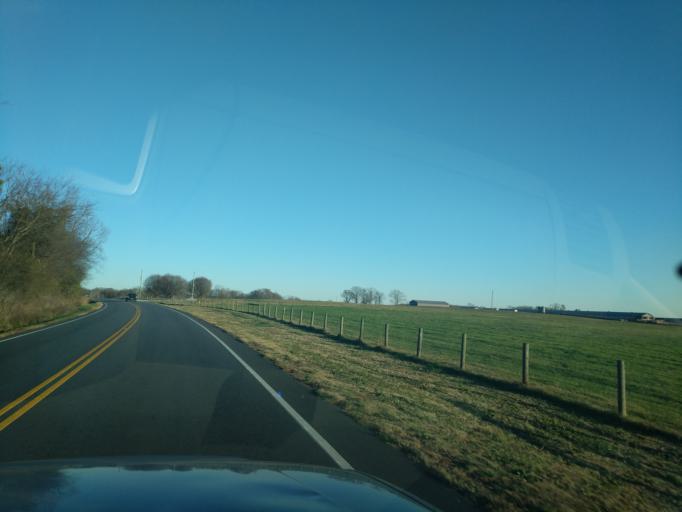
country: US
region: South Carolina
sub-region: Oconee County
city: Utica
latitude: 34.5838
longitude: -82.9439
